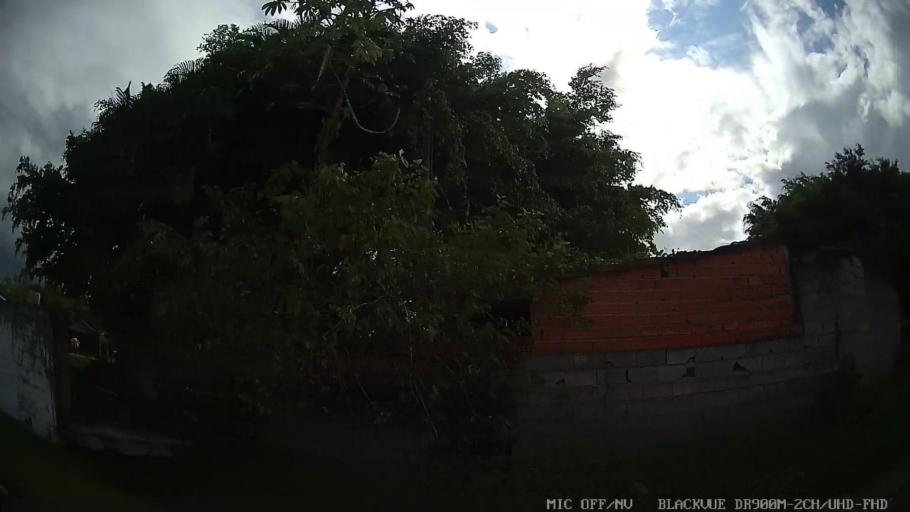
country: BR
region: Sao Paulo
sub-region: Caraguatatuba
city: Caraguatatuba
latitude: -23.6432
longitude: -45.4303
